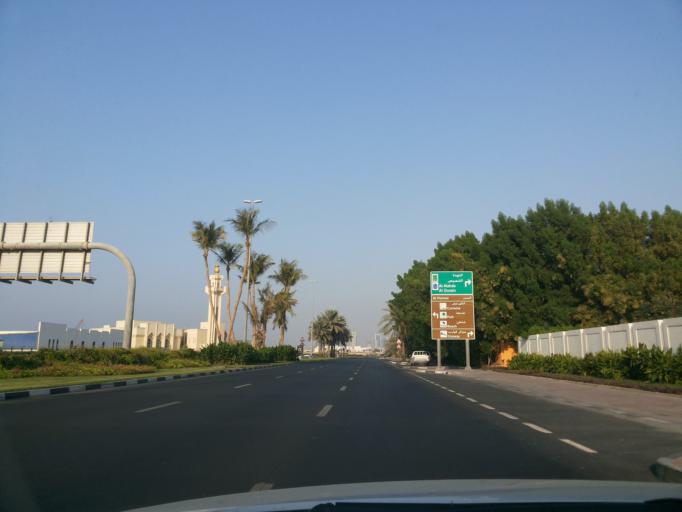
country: AE
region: Ash Shariqah
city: Sharjah
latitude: 25.2995
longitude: 55.3373
